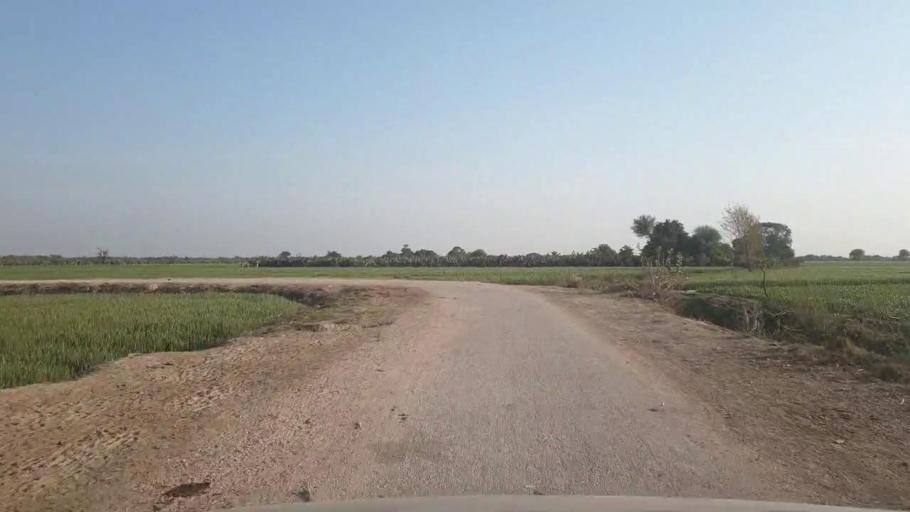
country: PK
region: Sindh
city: Chambar
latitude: 25.2569
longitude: 68.8882
